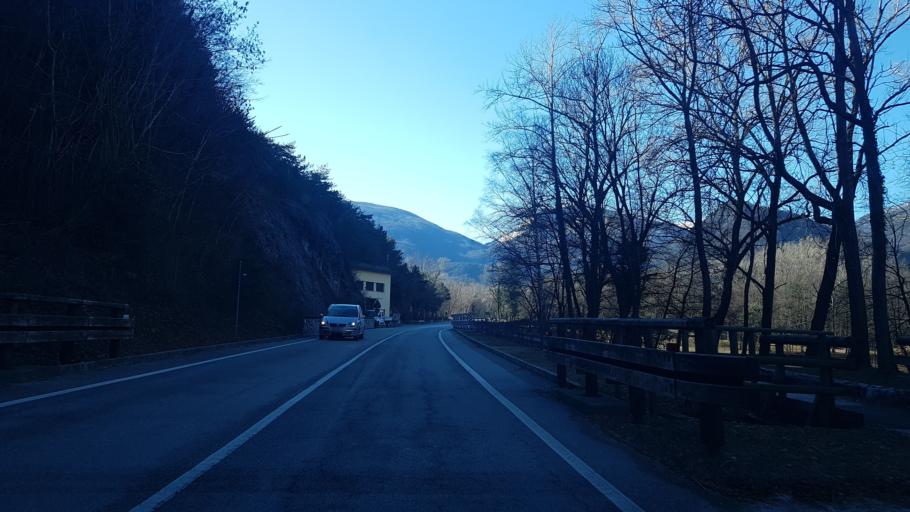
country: IT
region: Friuli Venezia Giulia
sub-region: Provincia di Udine
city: Bordano
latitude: 46.3186
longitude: 13.0685
